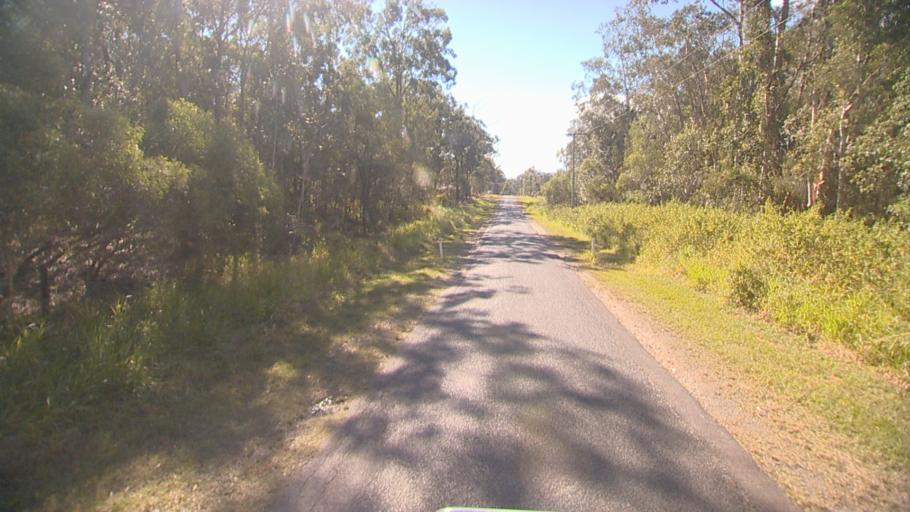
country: AU
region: Queensland
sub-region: Logan
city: Chambers Flat
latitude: -27.8081
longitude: 153.0823
